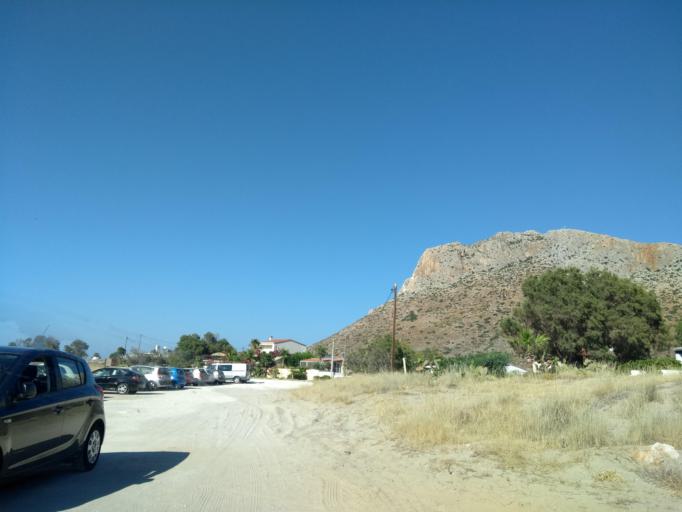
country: GR
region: Crete
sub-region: Nomos Chanias
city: Pithari
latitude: 35.5914
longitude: 24.0908
